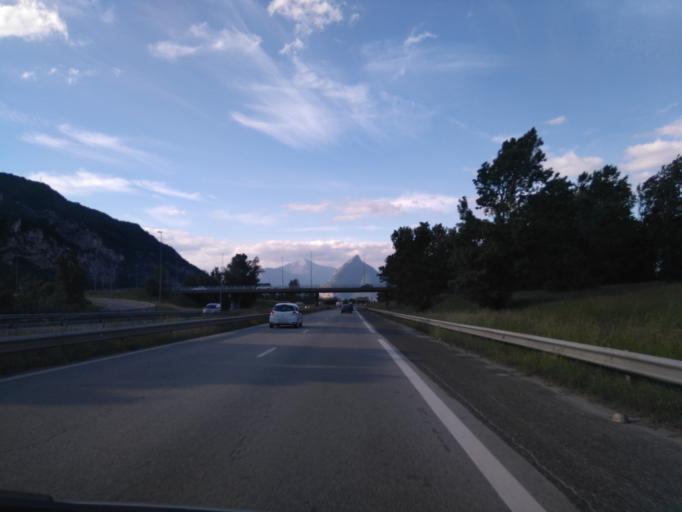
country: FR
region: Rhone-Alpes
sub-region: Departement de l'Isere
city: Le Pont-de-Claix
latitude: 45.1341
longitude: 5.6904
